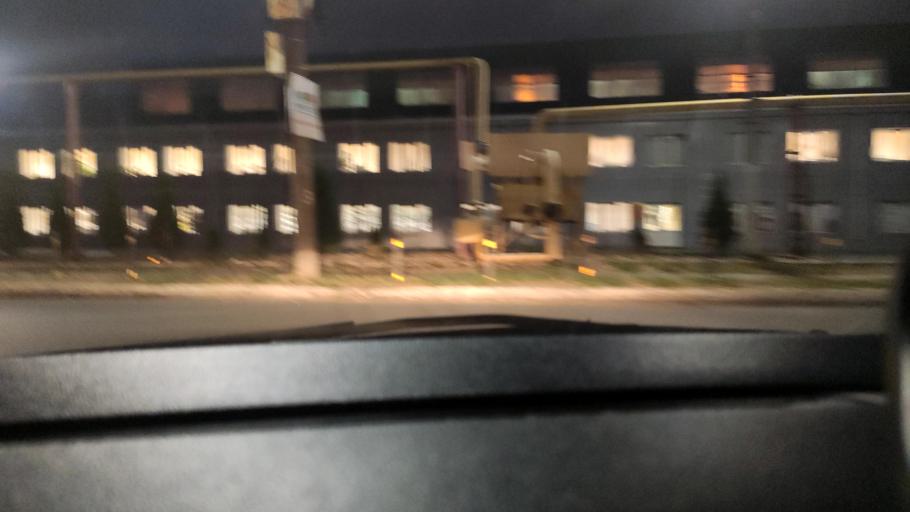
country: RU
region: Voronezj
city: Voronezh
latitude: 51.6872
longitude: 39.1698
